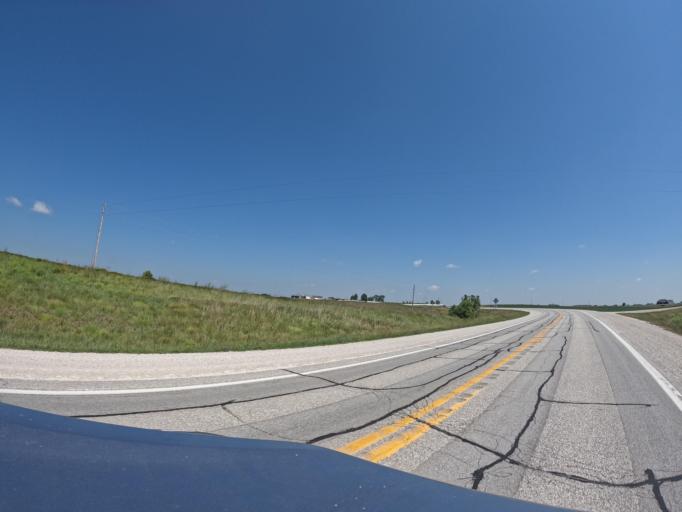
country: US
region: Iowa
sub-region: Keokuk County
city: Sigourney
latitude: 41.2473
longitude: -92.2065
